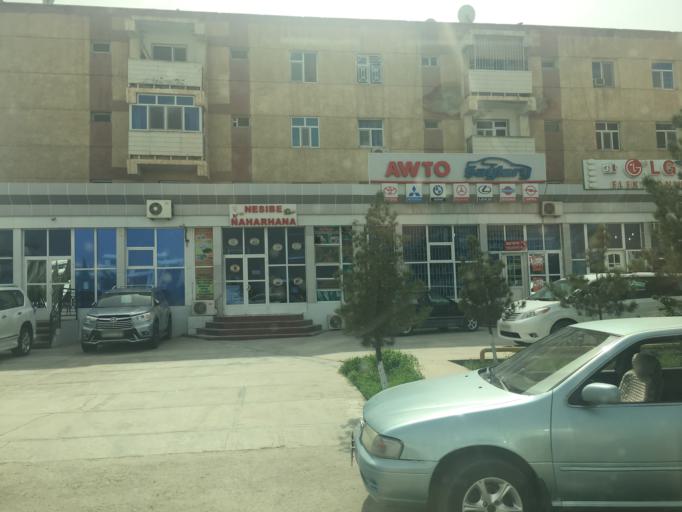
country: TM
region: Mary
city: Mary
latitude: 37.5990
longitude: 61.8730
